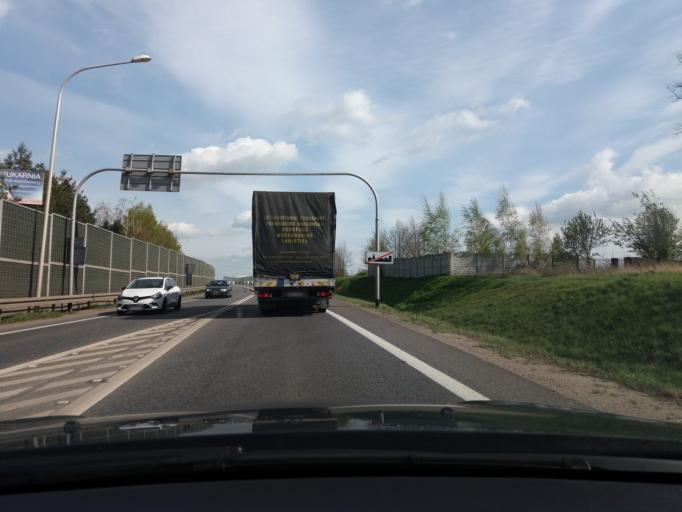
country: PL
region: Lower Silesian Voivodeship
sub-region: Powiat sredzki
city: Sroda Slaska
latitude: 51.1582
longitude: 16.5911
